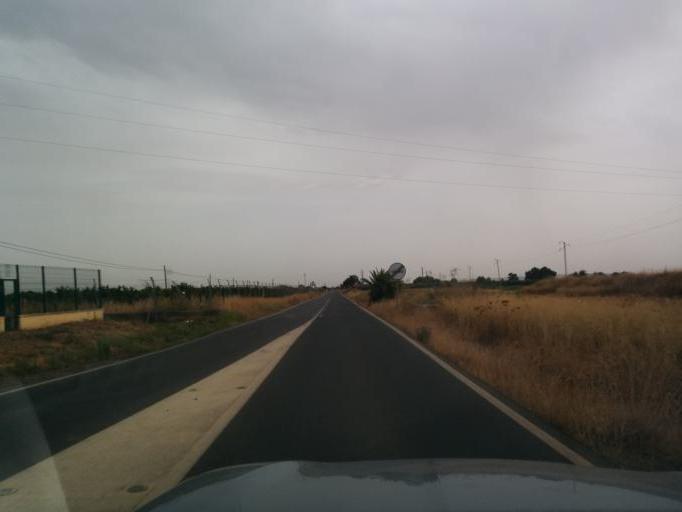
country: ES
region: Andalusia
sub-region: Provincia de Sevilla
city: Guillena
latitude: 37.5365
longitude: -6.0353
